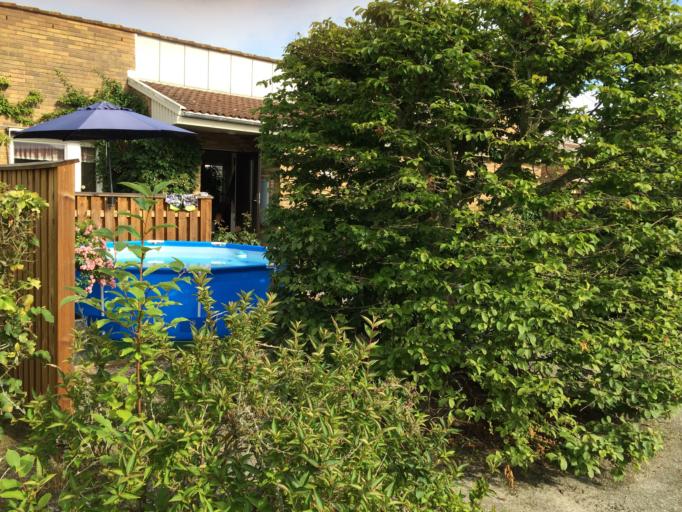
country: SE
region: Skane
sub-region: Vellinge Kommun
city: Skanor med Falsterbo
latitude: 55.4127
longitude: 12.8508
